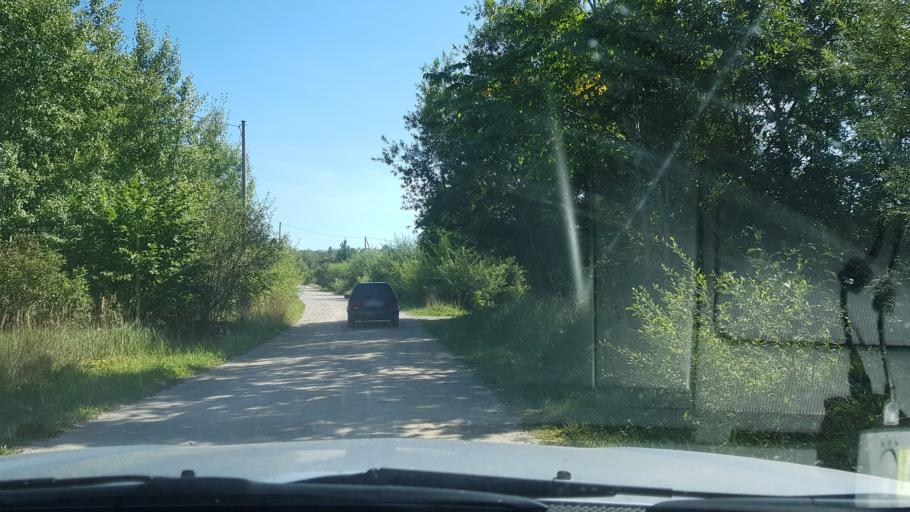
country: EE
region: Ida-Virumaa
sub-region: Sillamaee linn
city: Sillamae
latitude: 59.3722
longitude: 27.7903
